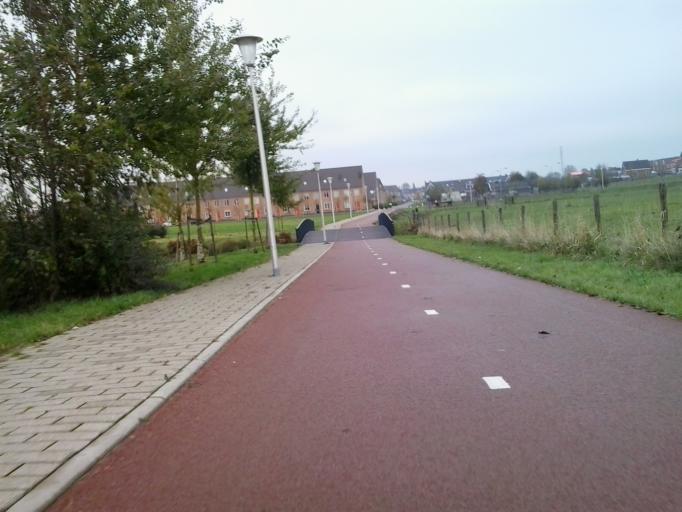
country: NL
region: South Holland
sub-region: Gemeente Lansingerland
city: Berkel en Rodenrijs
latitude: 52.0008
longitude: 4.4801
